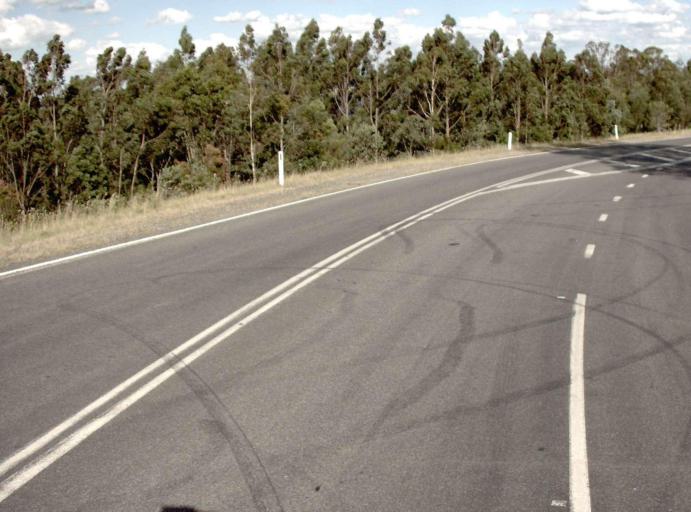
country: AU
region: Victoria
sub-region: Latrobe
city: Moe
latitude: -38.1968
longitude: 146.3259
